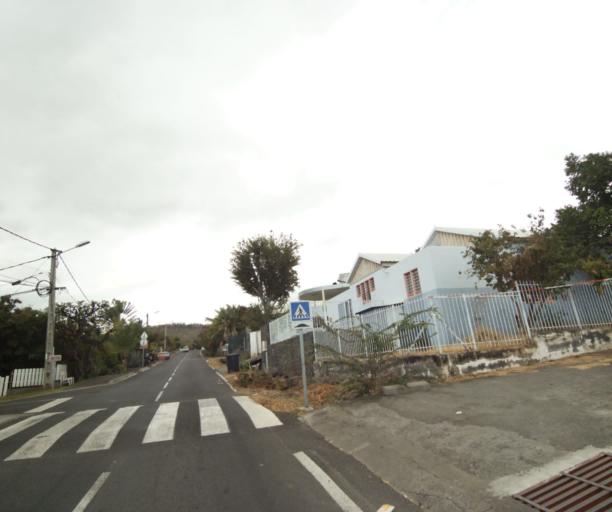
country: RE
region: Reunion
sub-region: Reunion
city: Saint-Paul
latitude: -21.0538
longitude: 55.2317
